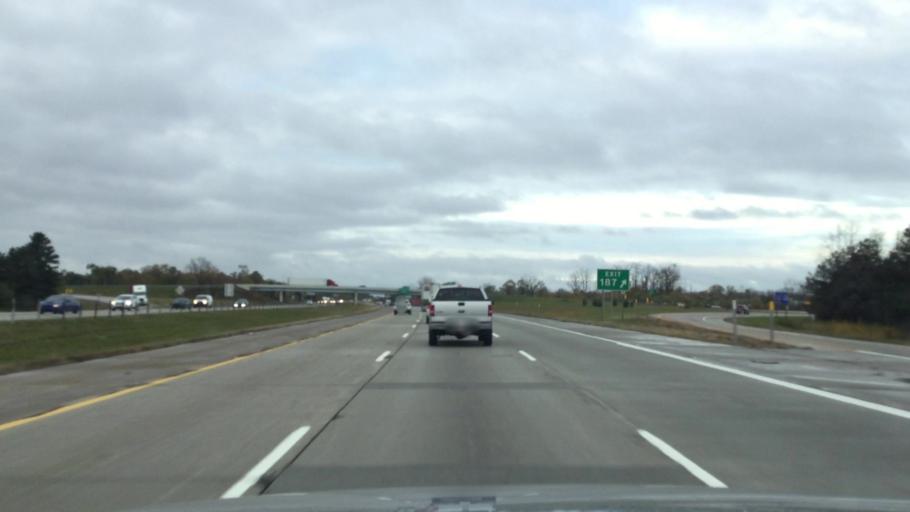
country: US
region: Michigan
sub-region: Wayne County
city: Belleville
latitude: 42.2189
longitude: -83.5408
